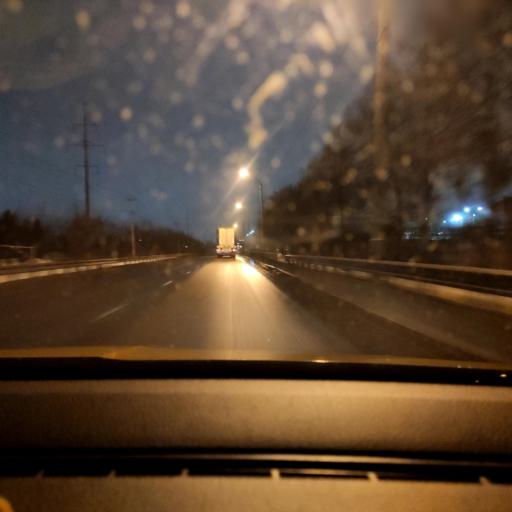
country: RU
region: Moskovskaya
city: Mosrentgen
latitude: 55.6143
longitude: 37.4608
